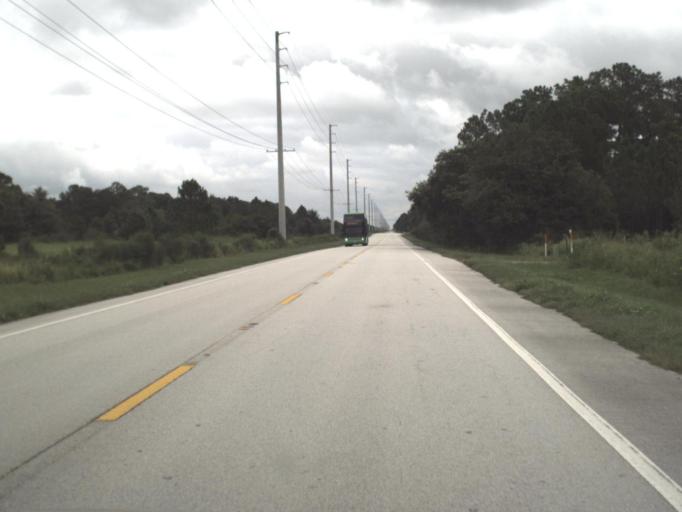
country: US
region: Florida
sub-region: Hardee County
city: Bowling Green
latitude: 27.5951
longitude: -82.0343
